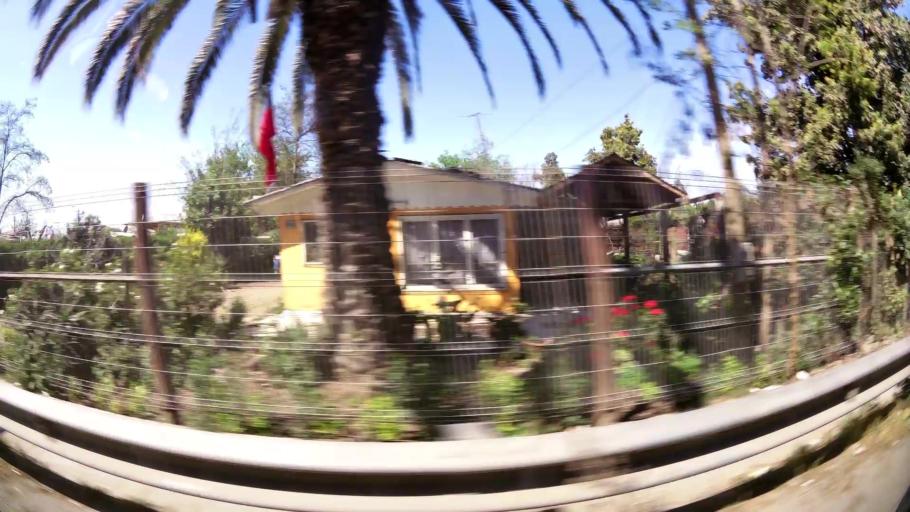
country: CL
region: Santiago Metropolitan
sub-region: Provincia de Talagante
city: Penaflor
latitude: -33.6147
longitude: -70.9066
